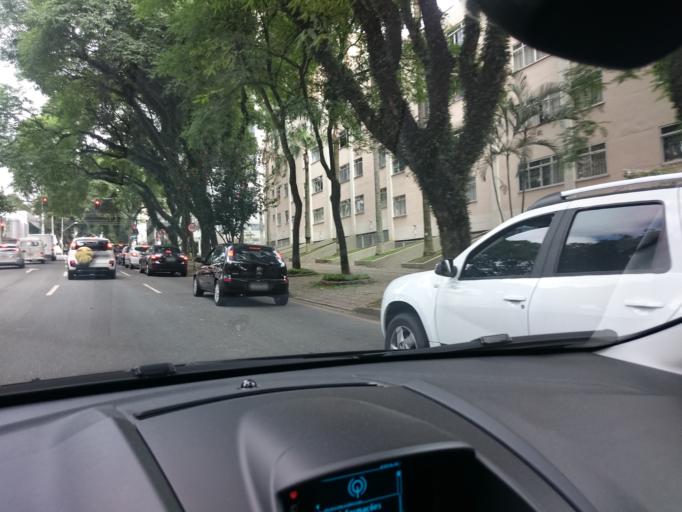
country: BR
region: Parana
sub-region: Curitiba
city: Curitiba
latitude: -25.4538
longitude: -49.2872
